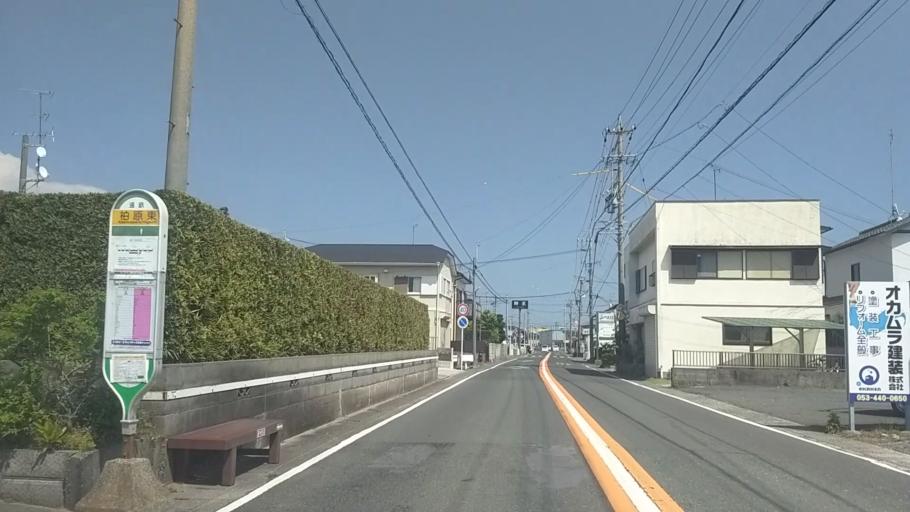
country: JP
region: Shizuoka
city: Hamamatsu
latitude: 34.6841
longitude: 137.6746
